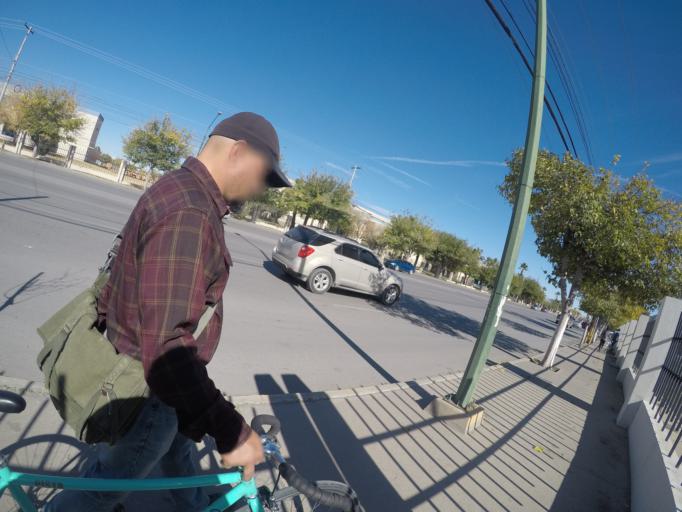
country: MX
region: Chihuahua
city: Ciudad Juarez
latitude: 31.7330
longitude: -106.4172
